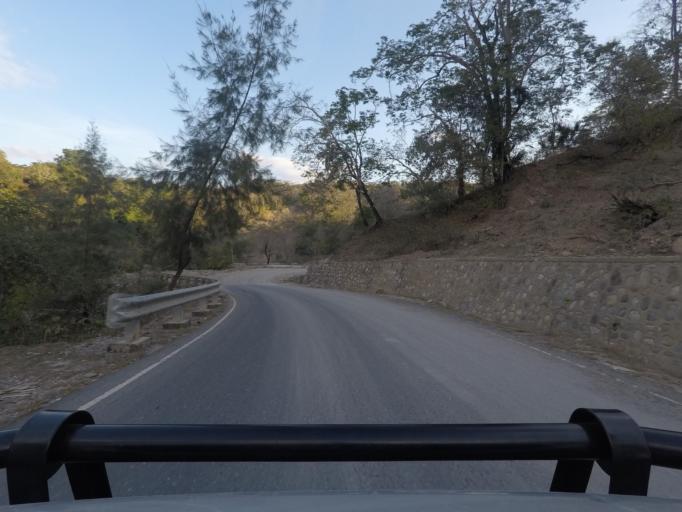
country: TL
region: Bobonaro
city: Maliana
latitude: -8.9490
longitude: 125.1006
